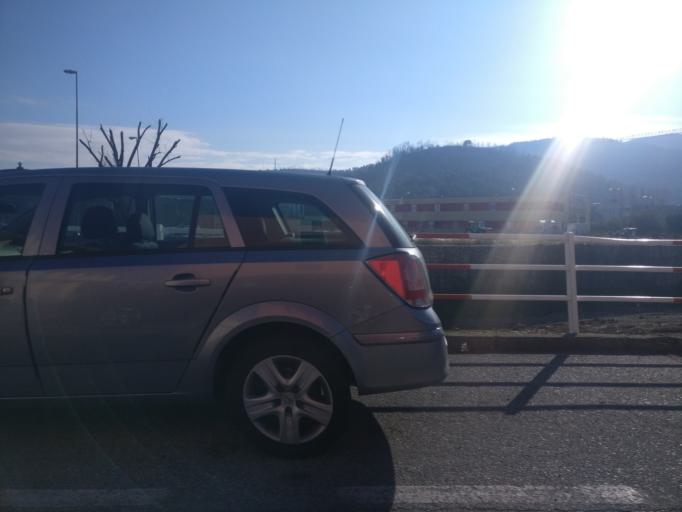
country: IT
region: Liguria
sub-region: Provincia di Savona
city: Vado Ligure
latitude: 44.2683
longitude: 8.4352
